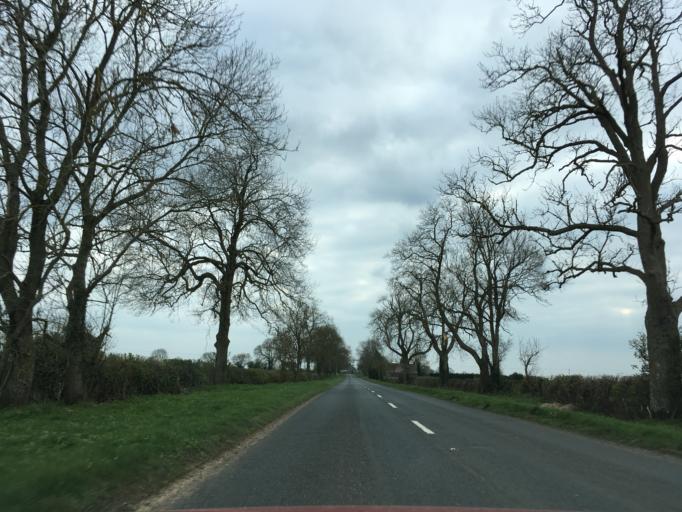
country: GB
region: England
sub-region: Gloucestershire
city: Northleach
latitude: 51.7764
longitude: -1.7987
